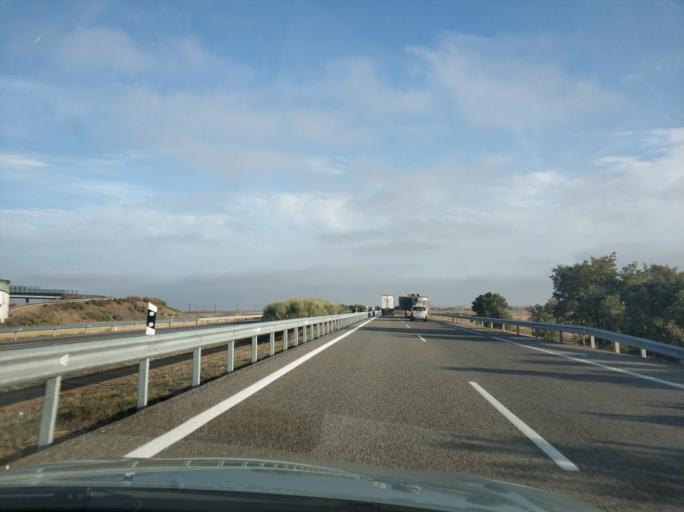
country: ES
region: Castille and Leon
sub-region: Provincia de Leon
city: Bercianos del Real Camino
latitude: 42.4089
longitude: -5.1873
